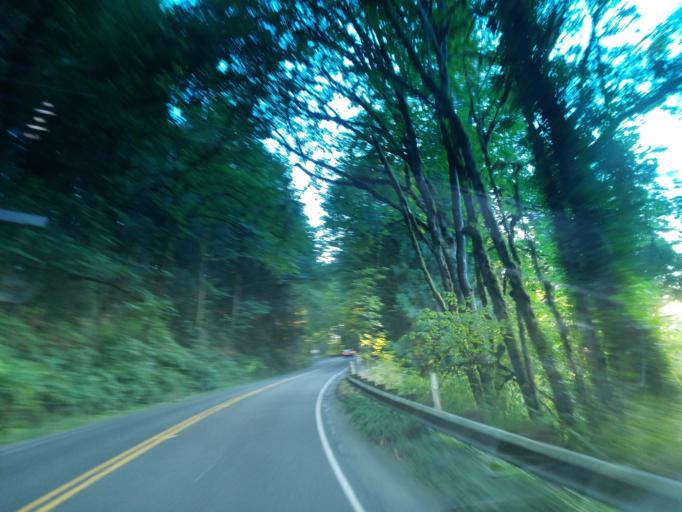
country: US
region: Washington
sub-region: King County
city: City of Sammamish
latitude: 47.6387
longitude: -122.0118
